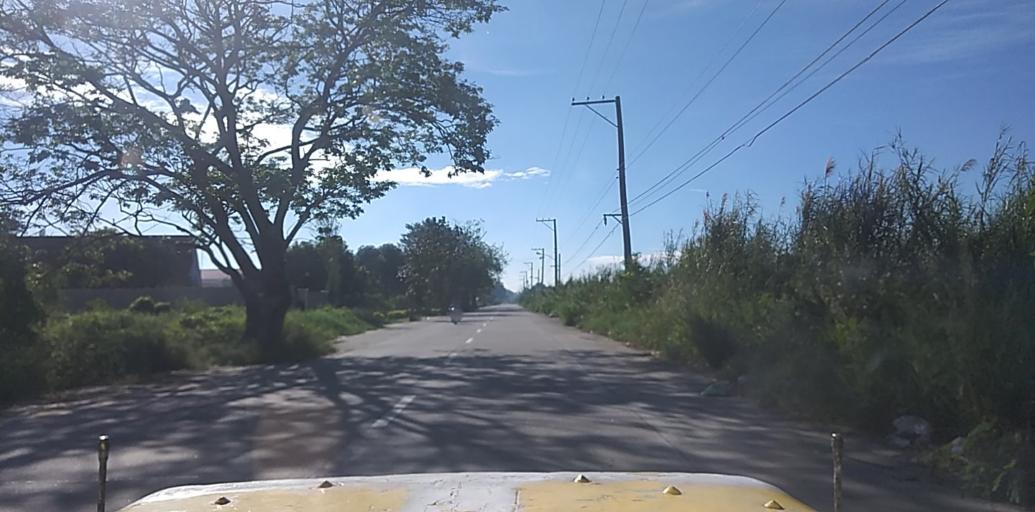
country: PH
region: Central Luzon
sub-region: Province of Pampanga
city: Anao
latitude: 15.1295
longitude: 120.6977
